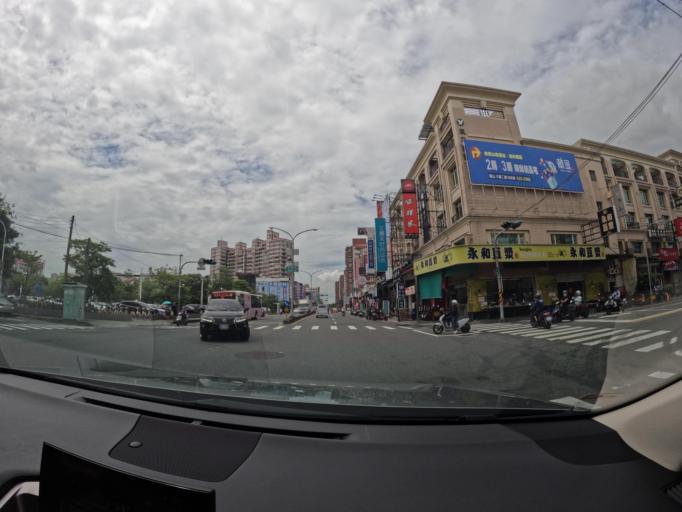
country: TW
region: Kaohsiung
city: Kaohsiung
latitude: 22.7920
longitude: 120.2960
